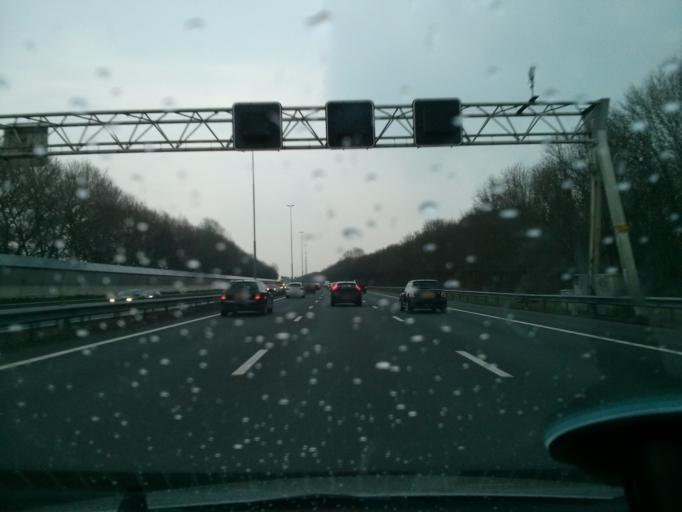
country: NL
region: North Holland
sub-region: Gemeente Ouder-Amstel
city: Ouderkerk aan de Amstel
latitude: 52.2919
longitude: 4.9003
